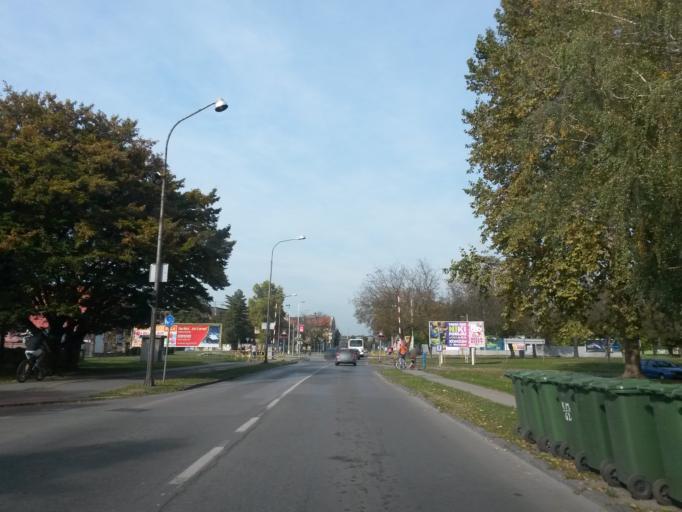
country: HR
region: Osjecko-Baranjska
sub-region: Grad Osijek
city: Osijek
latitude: 45.5536
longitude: 18.7048
